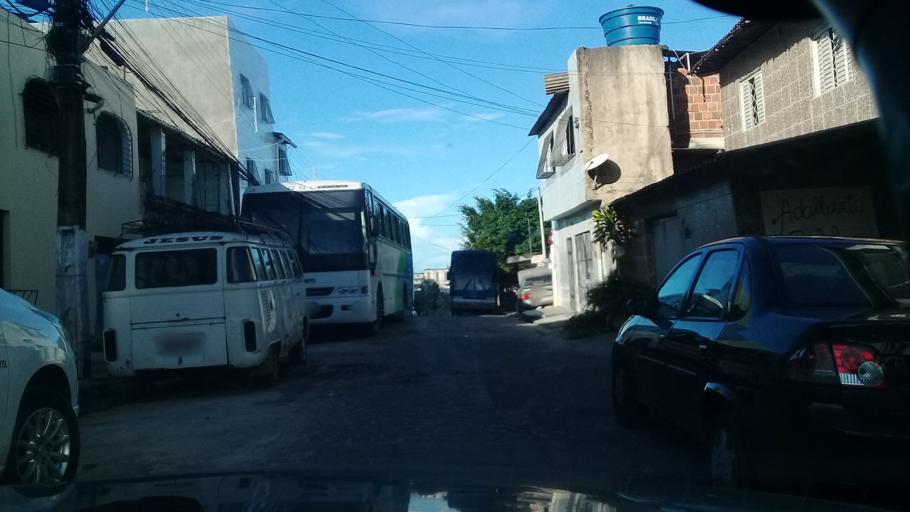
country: BR
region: Pernambuco
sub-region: Jaboatao Dos Guararapes
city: Jaboatao dos Guararapes
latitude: -8.1174
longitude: -34.9544
